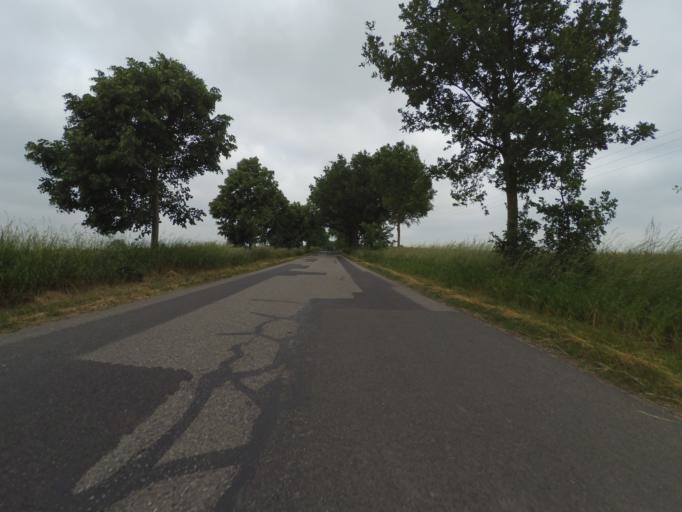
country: DE
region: Mecklenburg-Vorpommern
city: Lubz
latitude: 53.5140
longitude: 12.0396
